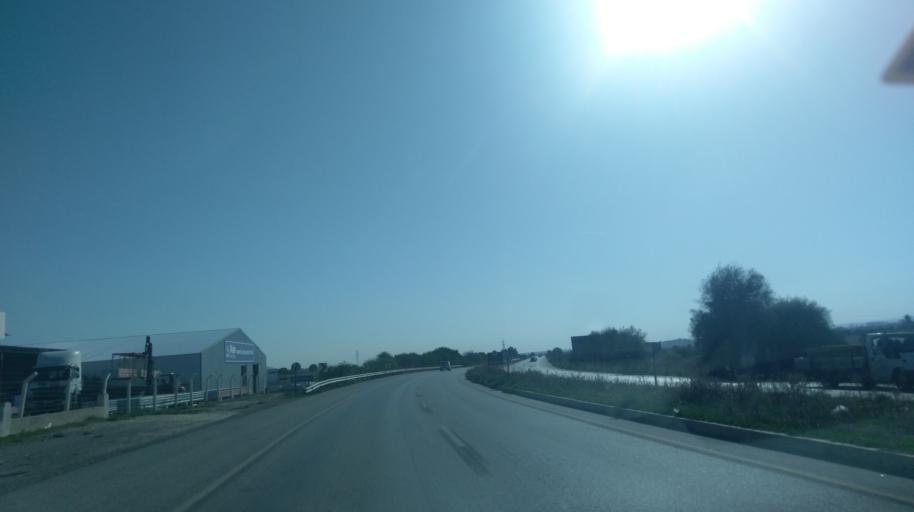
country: CY
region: Ammochostos
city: Lefkonoiko
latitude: 35.2073
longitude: 33.5948
